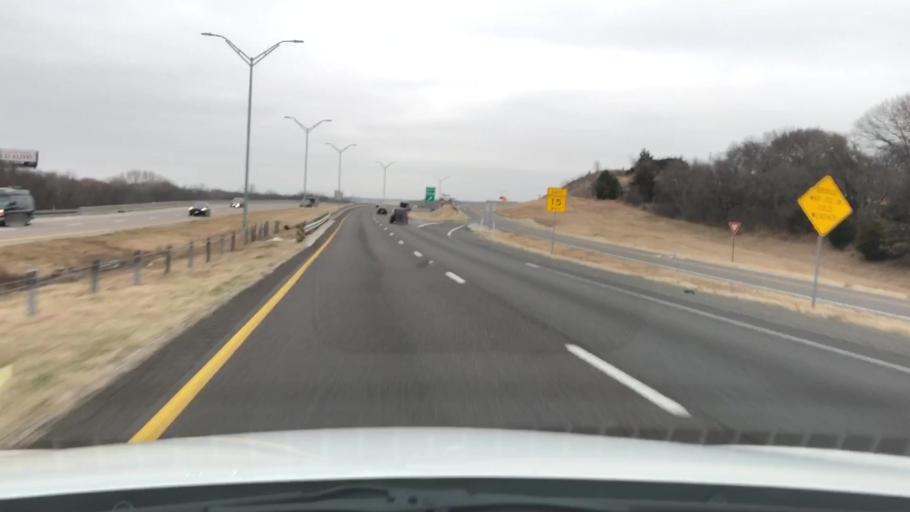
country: US
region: Texas
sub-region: Cooke County
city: Gainesville
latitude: 33.7221
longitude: -97.1612
